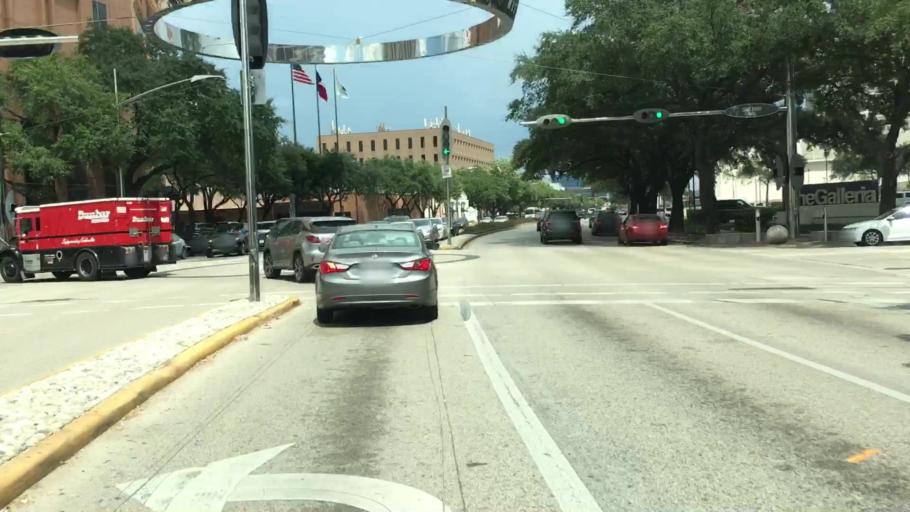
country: US
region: Texas
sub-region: Harris County
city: Bellaire
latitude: 29.7403
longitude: -95.4672
